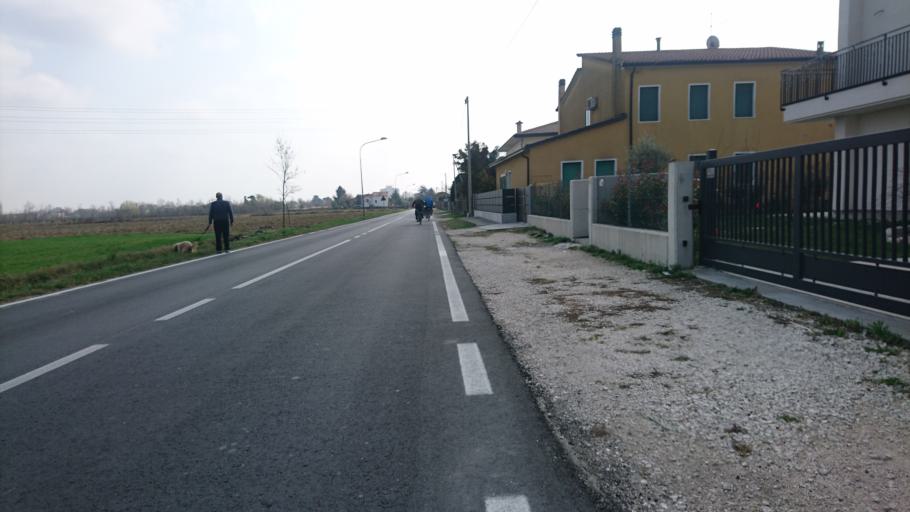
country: IT
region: Veneto
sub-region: Provincia di Padova
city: Abano Terme
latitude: 45.3614
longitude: 11.7651
